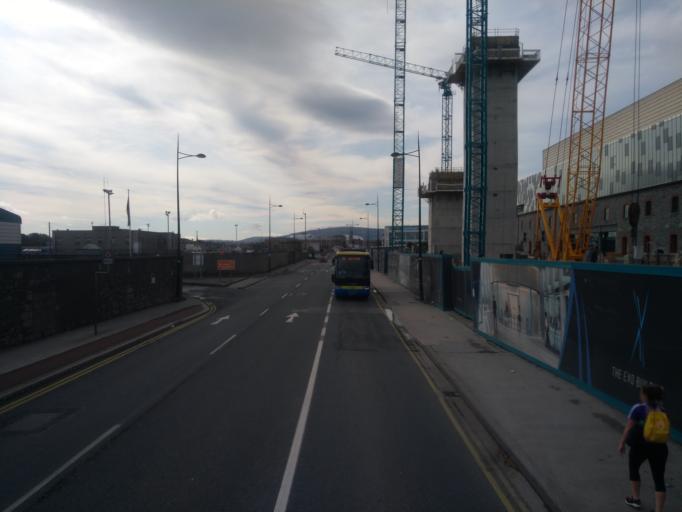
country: IE
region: Leinster
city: Ringsend
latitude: 53.3484
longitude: -6.2271
